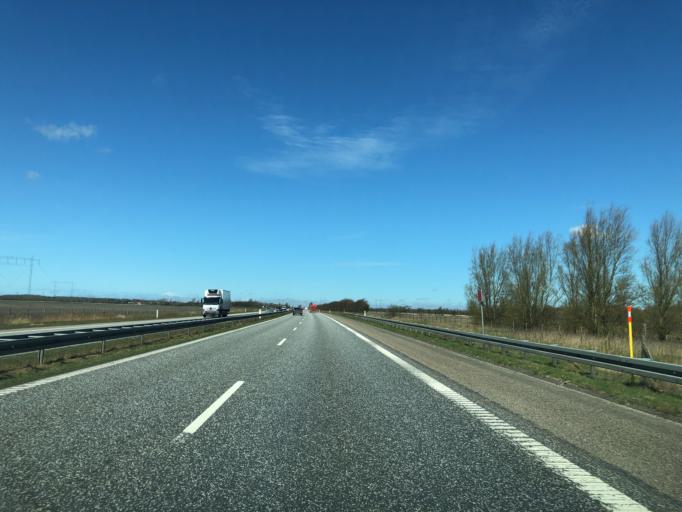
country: DK
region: North Denmark
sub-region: Alborg Kommune
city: Vestbjerg
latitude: 57.1042
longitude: 9.9616
